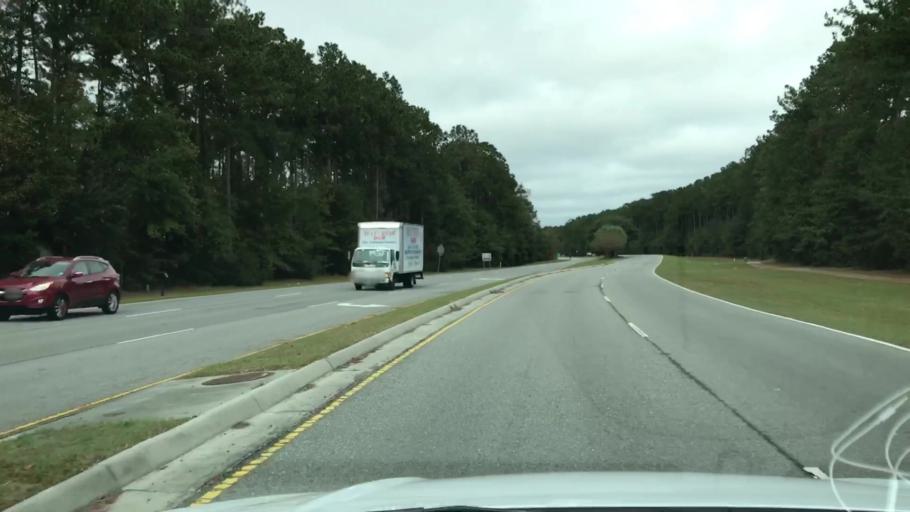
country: US
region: South Carolina
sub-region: Beaufort County
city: Bluffton
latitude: 32.2478
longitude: -80.9022
